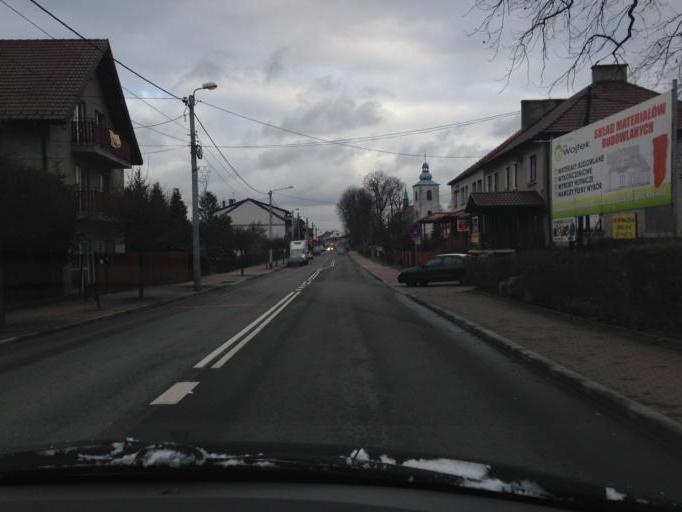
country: PL
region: Lesser Poland Voivodeship
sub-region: Powiat wielicki
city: Gdow
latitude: 49.9081
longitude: 20.1944
